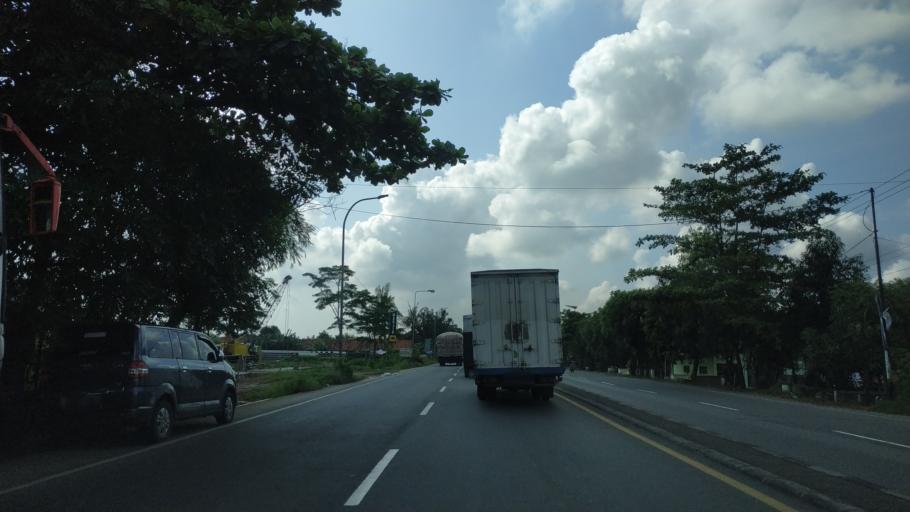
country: ID
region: Central Java
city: Comal
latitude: -6.8858
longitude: 109.5701
